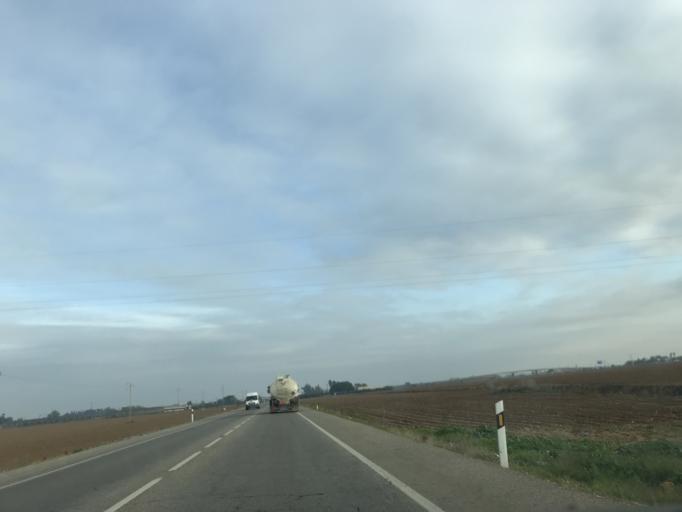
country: ES
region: Andalusia
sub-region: Provincia de Sevilla
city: La Rinconada
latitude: 37.4613
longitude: -5.9737
